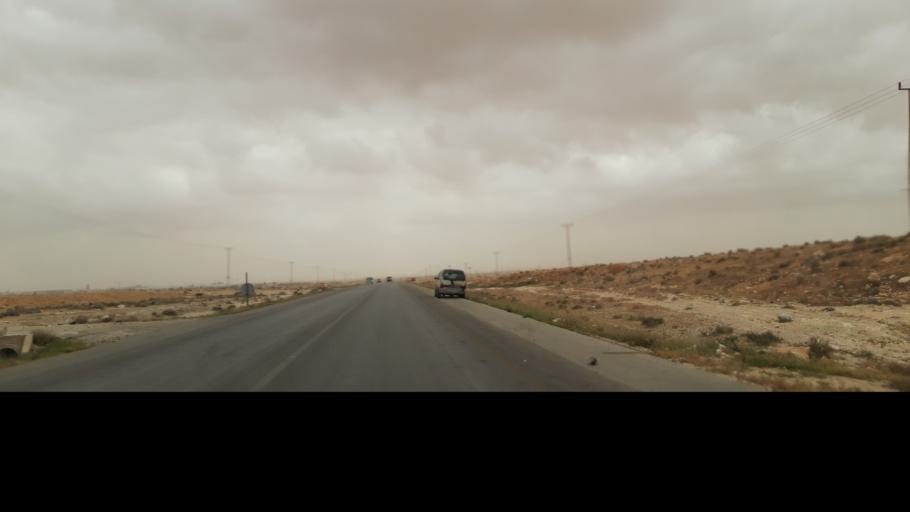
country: JO
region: Amman
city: Sahab
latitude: 31.7990
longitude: 36.1808
